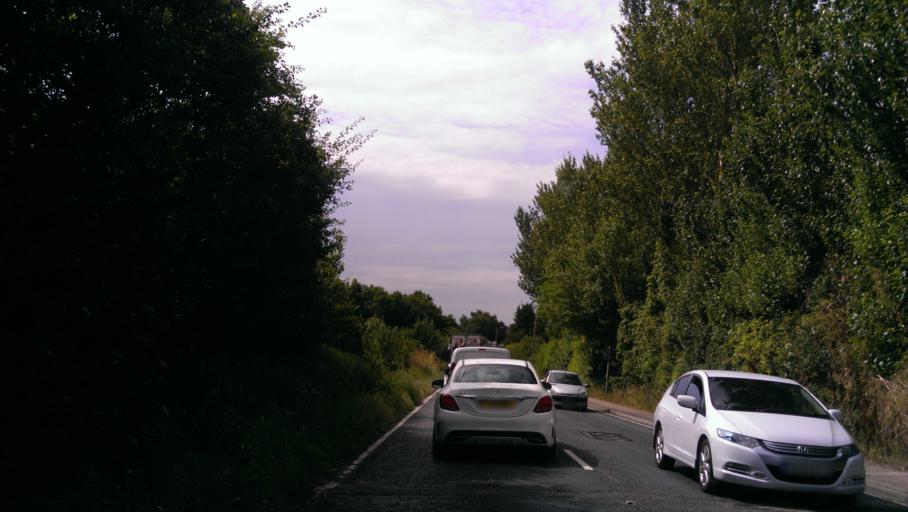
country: GB
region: England
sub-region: Kent
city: Teynham
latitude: 51.3251
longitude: 0.8105
